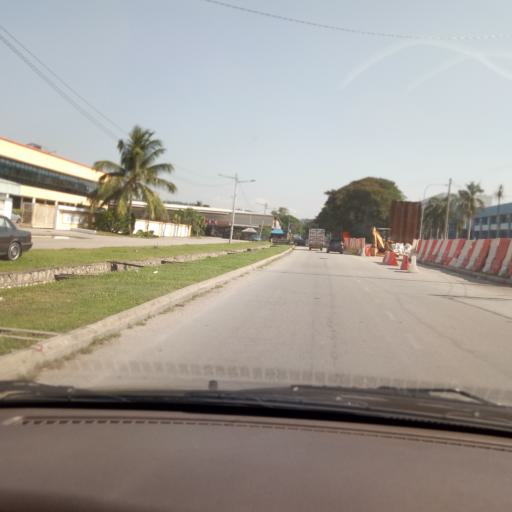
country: MY
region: Selangor
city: Kampong Baharu Balakong
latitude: 3.0243
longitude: 101.7646
